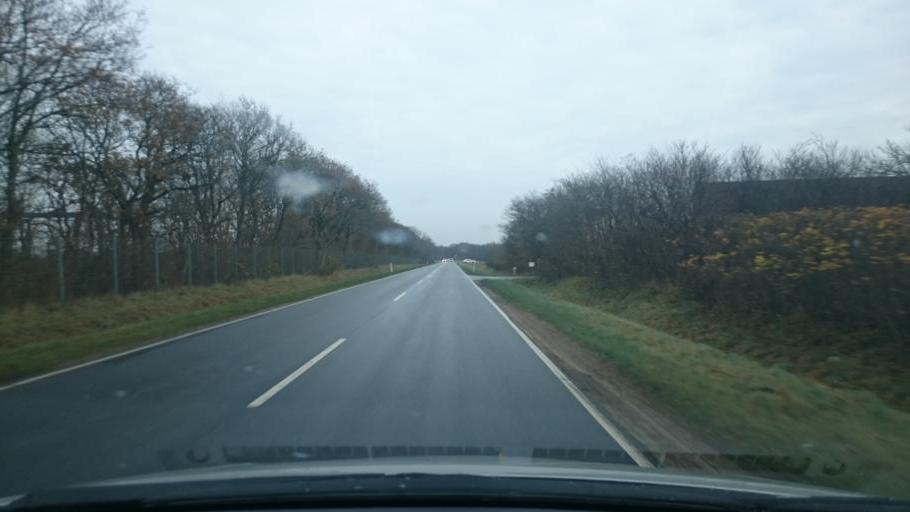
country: DK
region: South Denmark
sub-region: Esbjerg Kommune
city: Ribe
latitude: 55.3324
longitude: 8.8664
